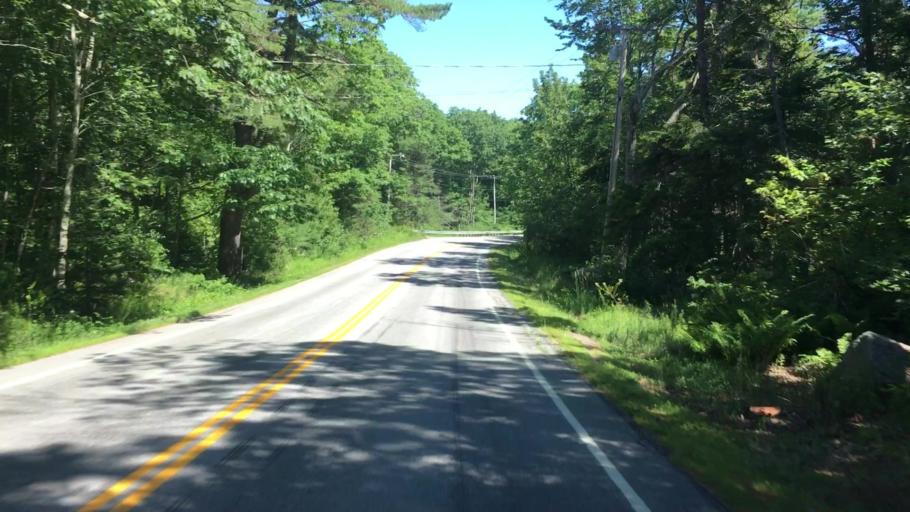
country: US
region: Maine
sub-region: Hancock County
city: Sedgwick
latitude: 44.3456
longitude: -68.6735
